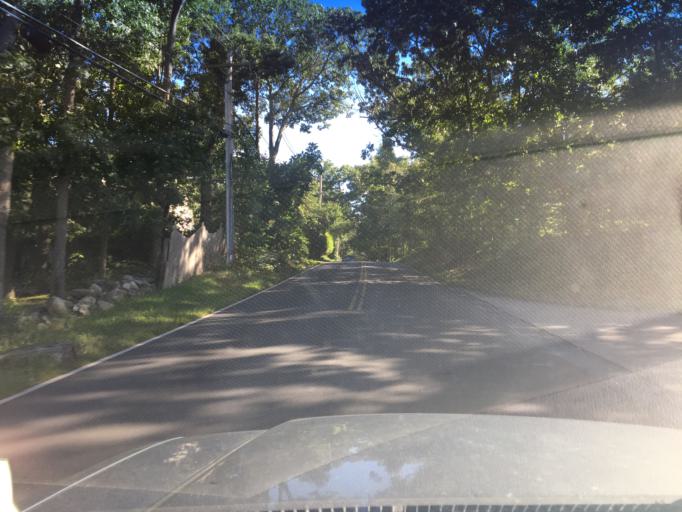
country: US
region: Massachusetts
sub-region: Middlesex County
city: Holliston
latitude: 42.1731
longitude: -71.4114
